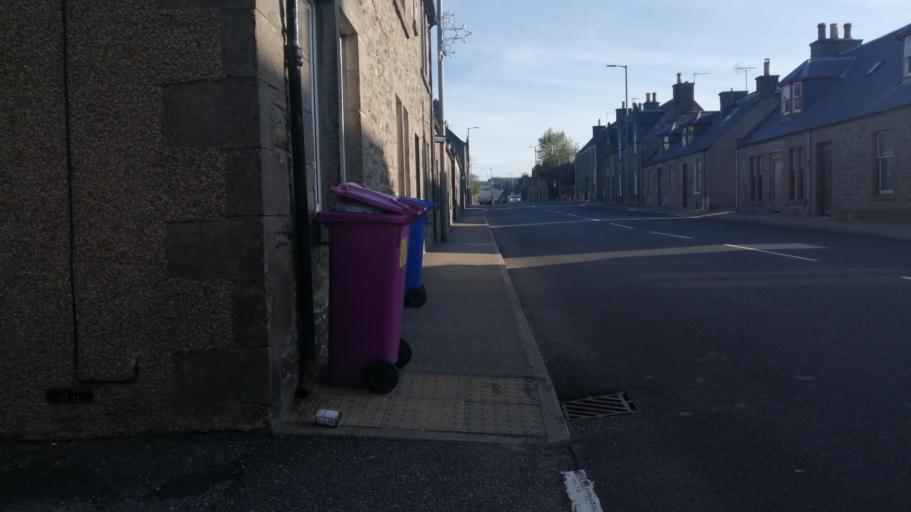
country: GB
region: Scotland
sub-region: Moray
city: Keith
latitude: 57.5405
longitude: -2.9483
